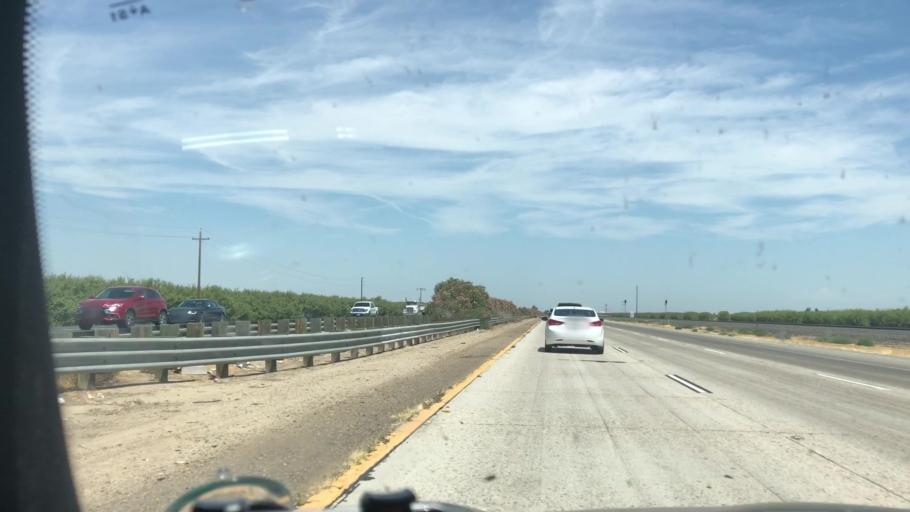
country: US
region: California
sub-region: Kern County
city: McFarland
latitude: 35.6238
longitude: -119.2144
